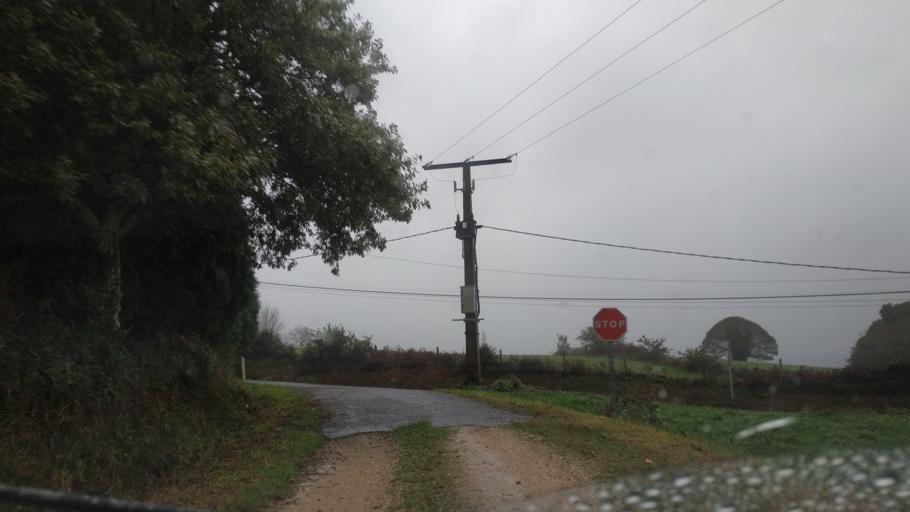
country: ES
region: Galicia
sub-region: Provincia da Coruna
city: Negreira
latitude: 42.9100
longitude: -8.7626
